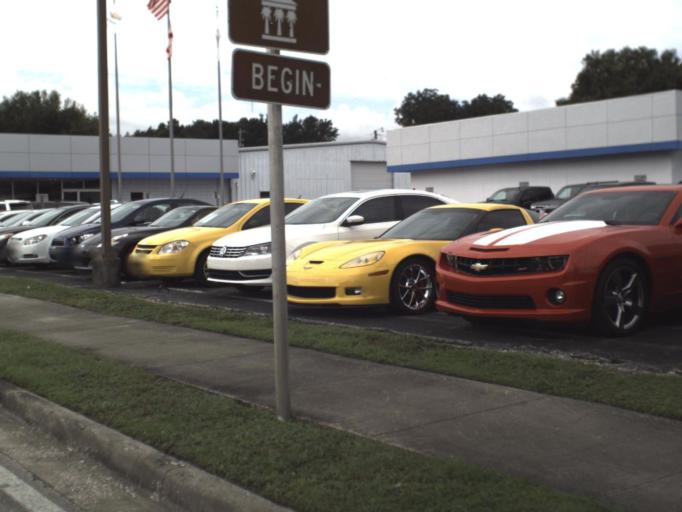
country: US
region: Florida
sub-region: Polk County
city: Fort Meade
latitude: 27.7551
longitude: -81.8016
